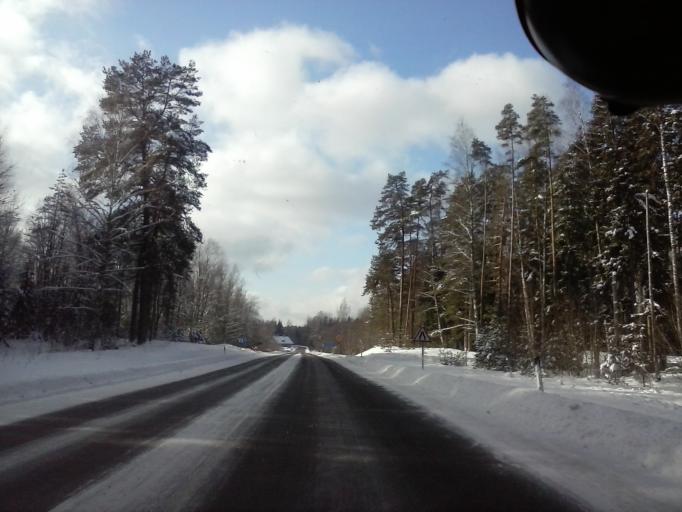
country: EE
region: Viljandimaa
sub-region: Moisakuela linn
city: Moisakula
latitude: 58.2463
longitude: 25.1454
